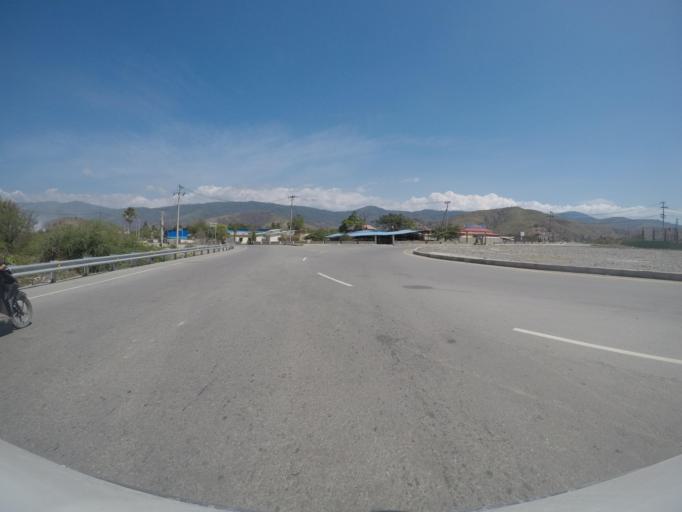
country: TL
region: Dili
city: Dili
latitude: -8.5681
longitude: 125.4911
